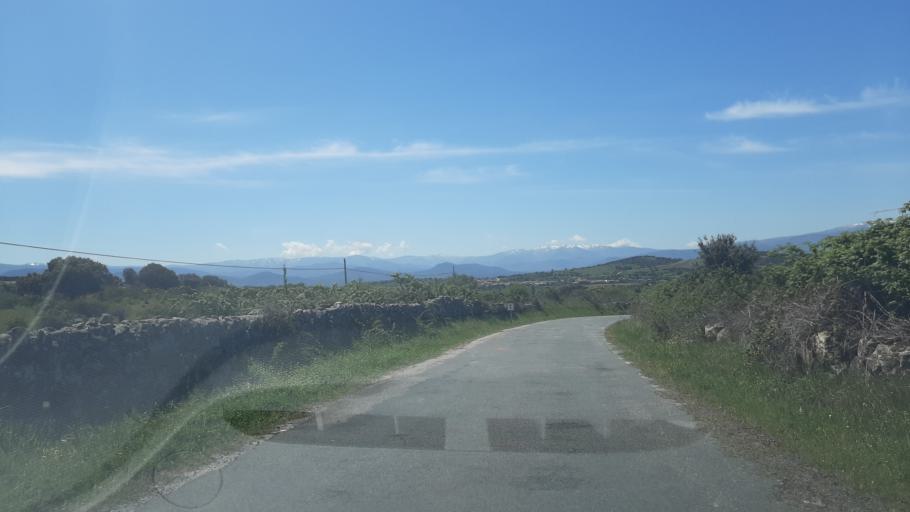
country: ES
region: Castille and Leon
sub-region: Provincia de Avila
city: Narrillos del Alamo
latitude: 40.5547
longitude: -5.4409
